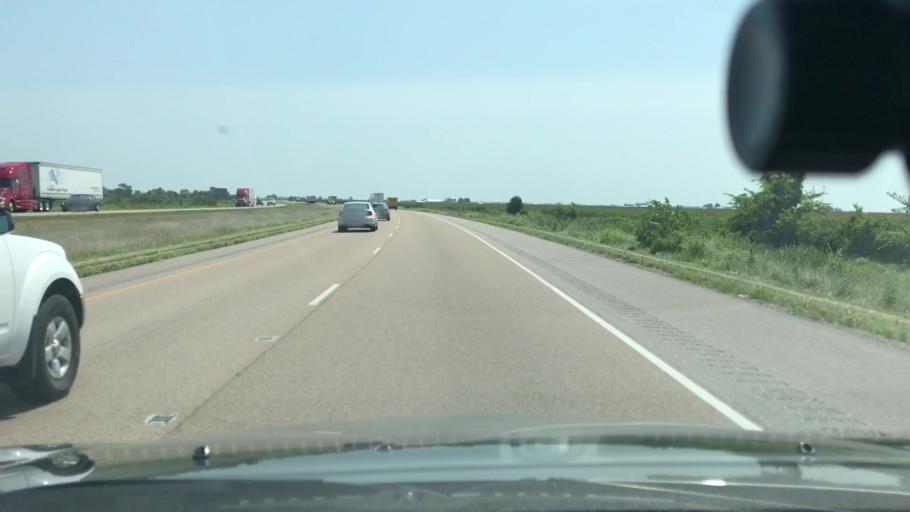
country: US
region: Illinois
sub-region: Washington County
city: Okawville
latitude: 38.4318
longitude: -89.5131
